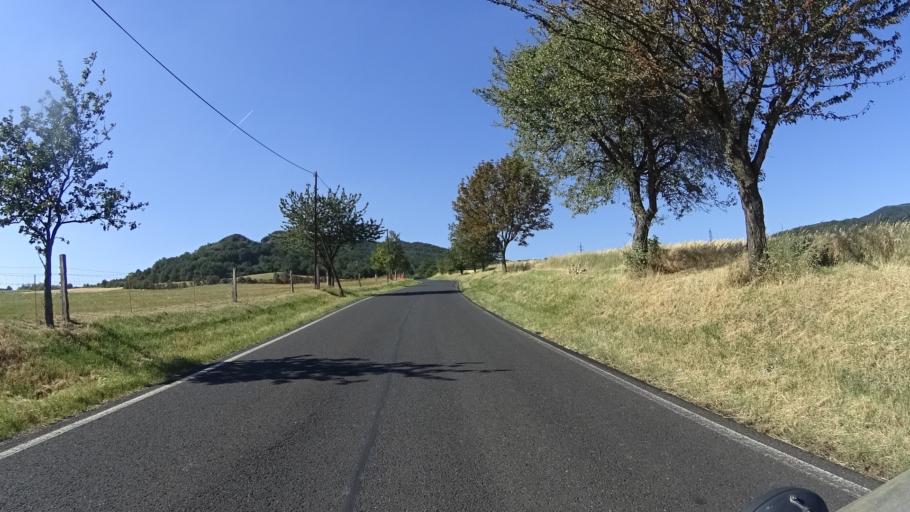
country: CZ
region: Ustecky
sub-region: Okres Litomerice
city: Litomerice
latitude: 50.5586
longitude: 14.1224
